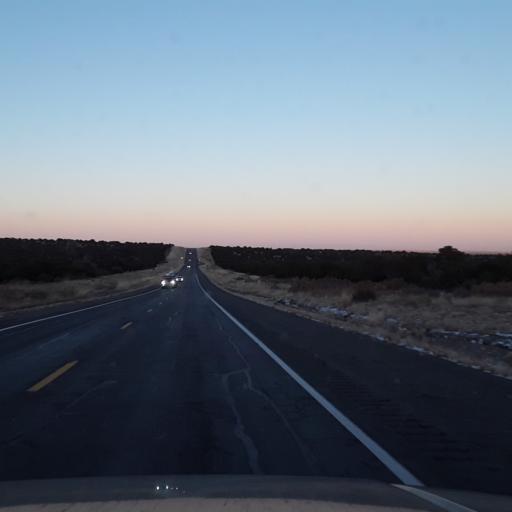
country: US
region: New Mexico
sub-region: Torrance County
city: Estancia
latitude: 34.5243
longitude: -105.3281
